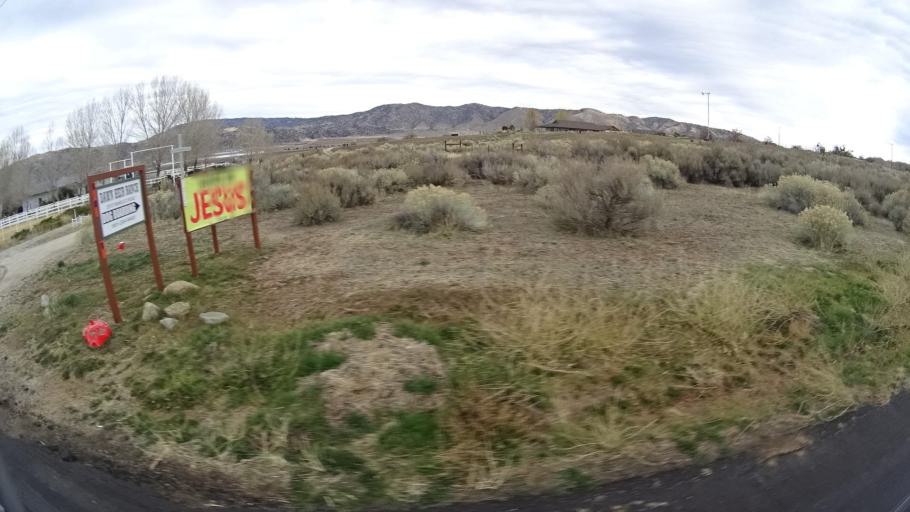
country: US
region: California
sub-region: Kern County
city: Stallion Springs
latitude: 35.0943
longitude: -118.5881
